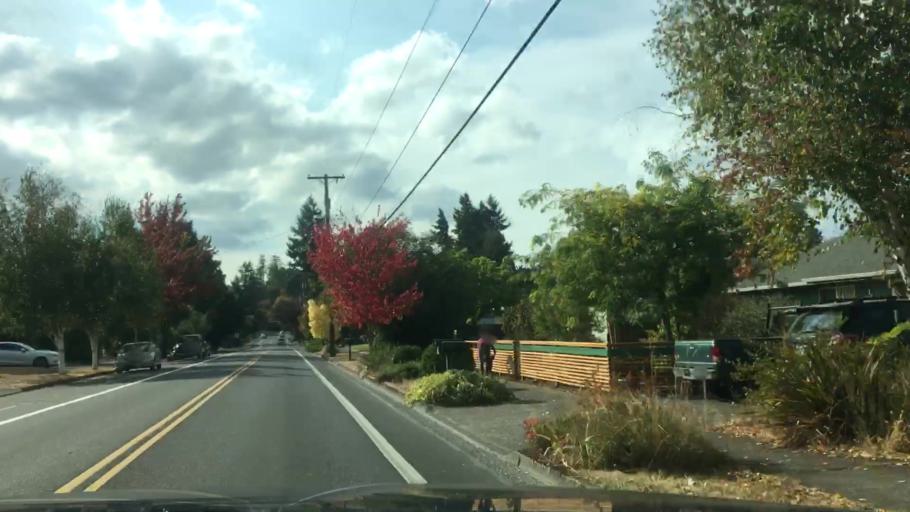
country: US
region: Oregon
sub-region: Lane County
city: Eugene
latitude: 44.0841
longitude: -123.0891
